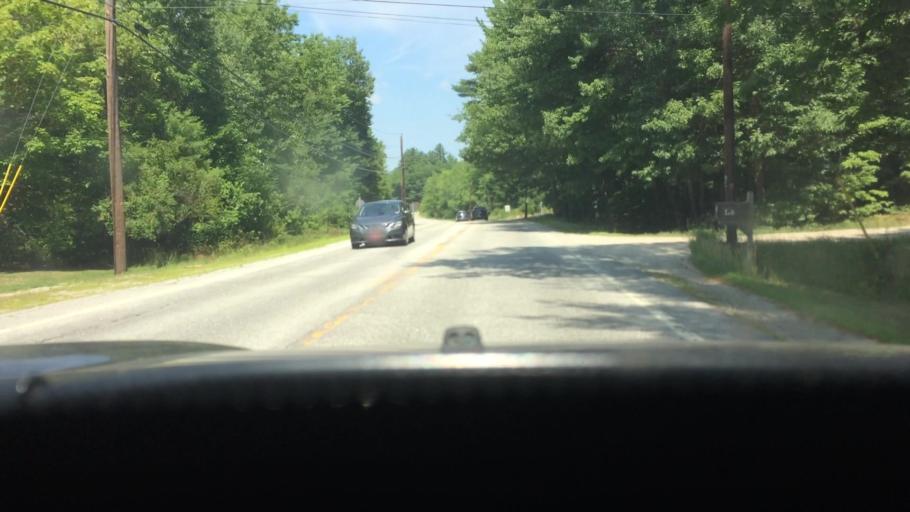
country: US
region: Maine
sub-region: Androscoggin County
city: Mechanic Falls
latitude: 44.1136
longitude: -70.4234
